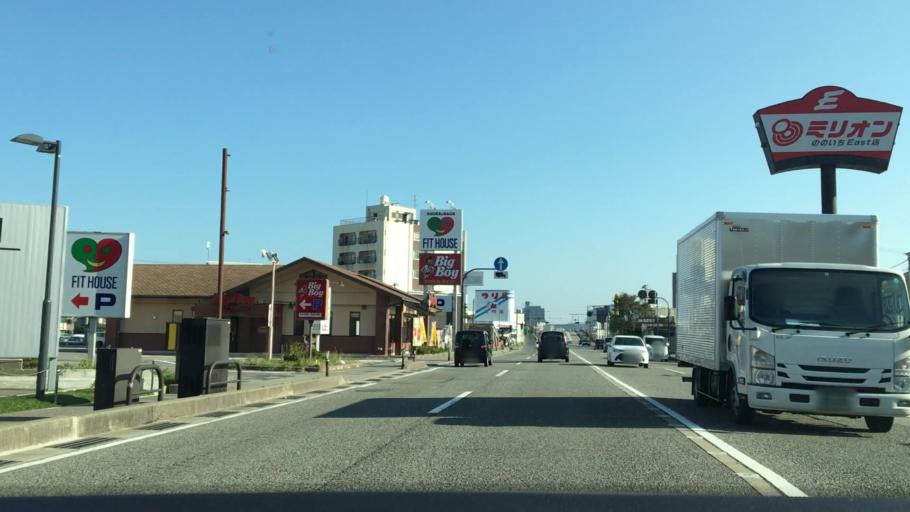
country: JP
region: Ishikawa
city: Nonoichi
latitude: 36.5373
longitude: 136.6184
